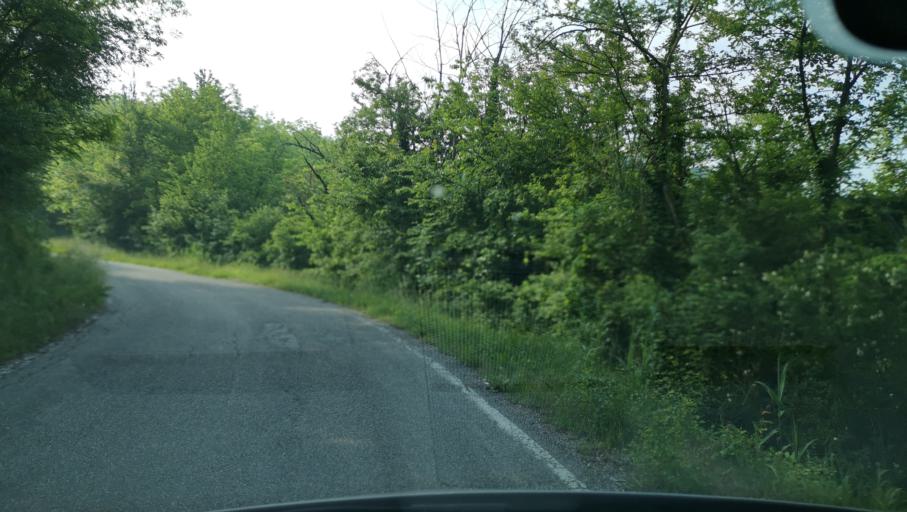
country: IT
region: Piedmont
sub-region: Provincia di Alessandria
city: Villadeati
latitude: 45.0806
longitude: 8.1821
